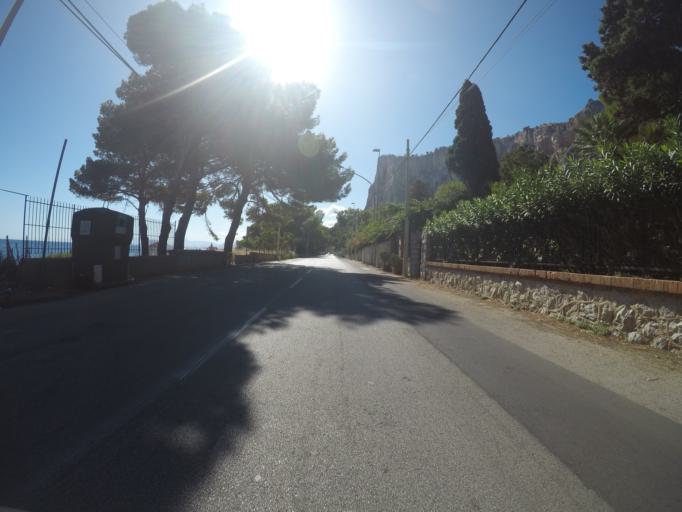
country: IT
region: Sicily
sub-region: Palermo
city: Palermo
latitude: 38.1895
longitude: 13.3591
